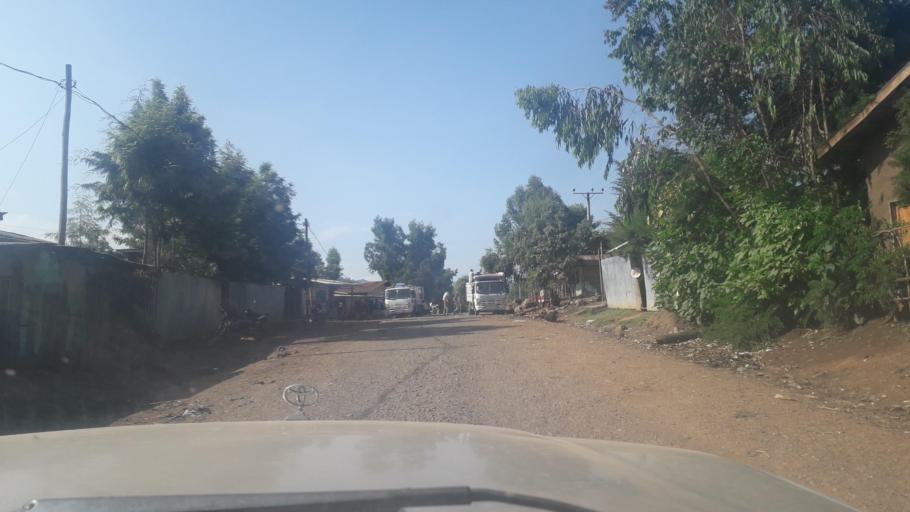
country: ET
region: Oromiya
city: Jima
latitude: 7.3730
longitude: 36.8708
